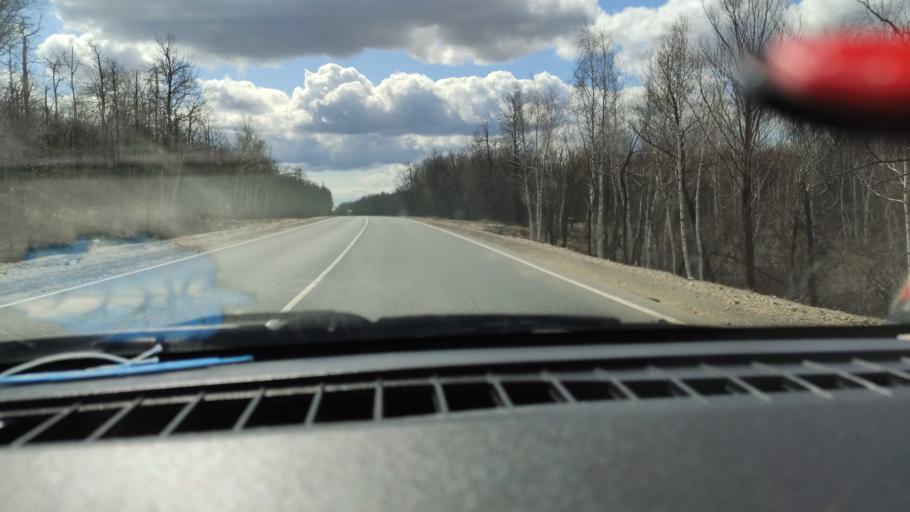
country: RU
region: Saratov
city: Khvalynsk
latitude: 52.4721
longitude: 48.0151
